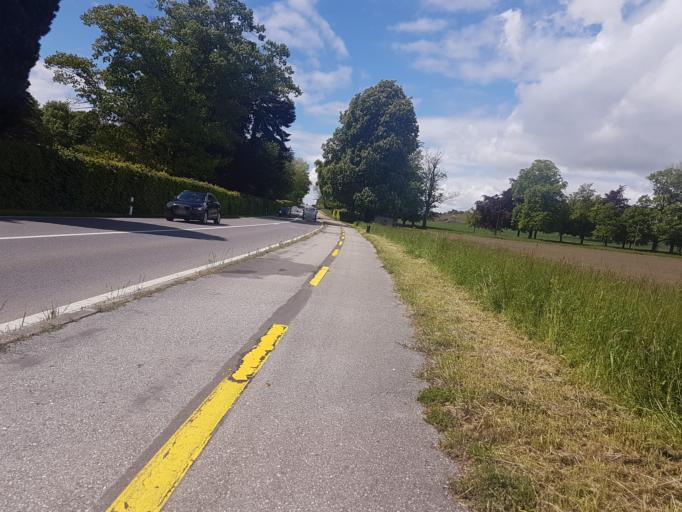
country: CH
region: Vaud
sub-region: Nyon District
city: Rolle
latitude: 46.4438
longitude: 6.3189
